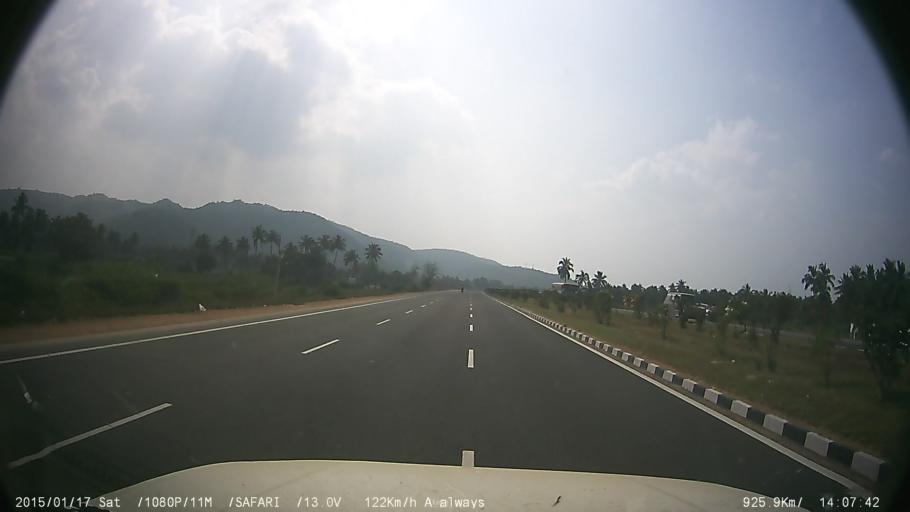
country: IN
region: Tamil Nadu
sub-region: Vellore
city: Ambur
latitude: 12.8279
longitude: 78.7724
